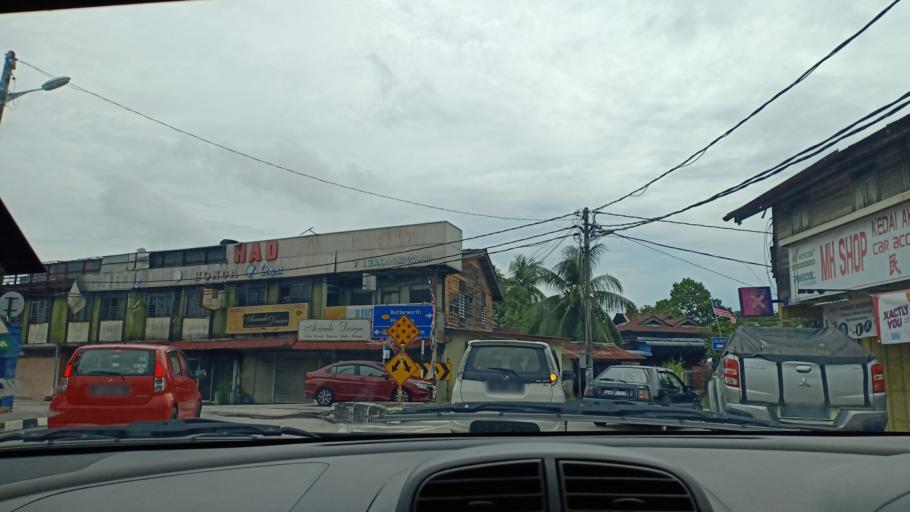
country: MY
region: Penang
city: Bukit Mertajam
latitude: 5.4034
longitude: 100.4644
